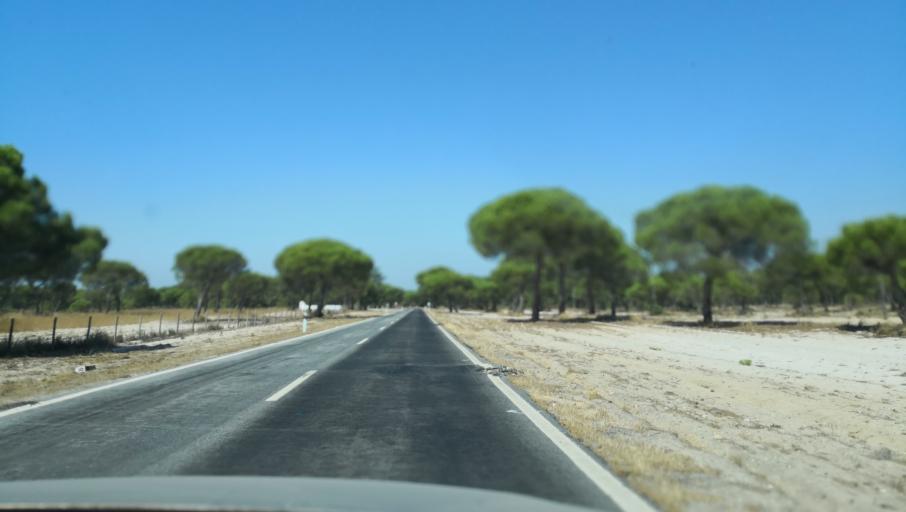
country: PT
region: Setubal
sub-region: Alcacer do Sal
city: Alcacer do Sal
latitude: 38.3904
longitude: -8.5691
